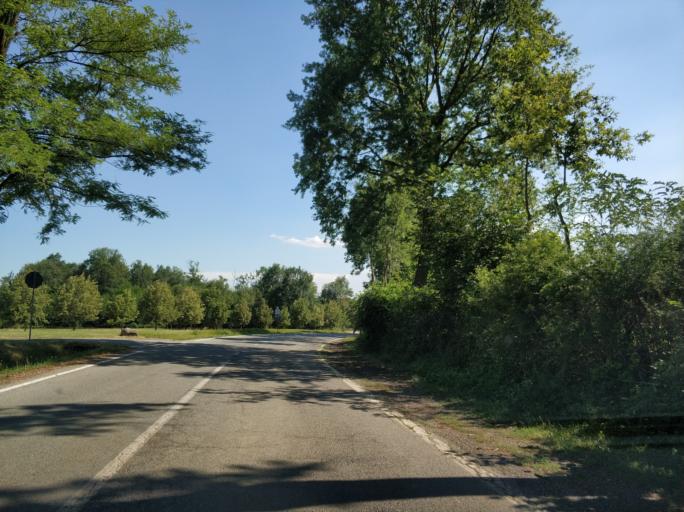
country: IT
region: Piedmont
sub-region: Provincia di Torino
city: San Carlo Canavese
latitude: 45.2546
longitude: 7.6127
